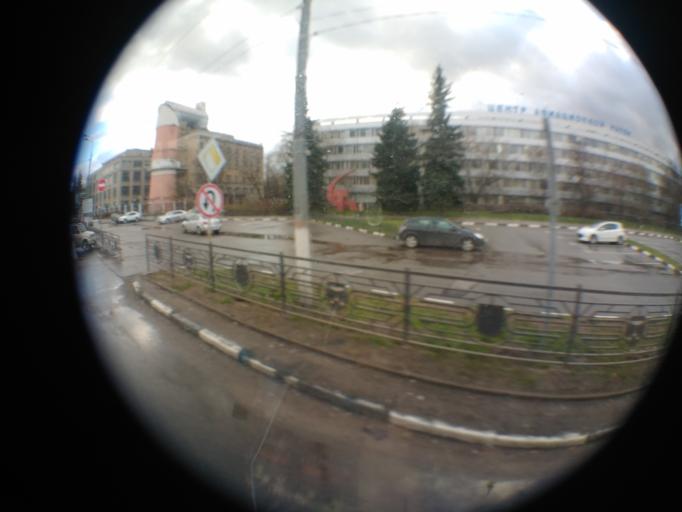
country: RU
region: Moskovskaya
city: Zhukovskiy
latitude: 55.5958
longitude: 38.1135
